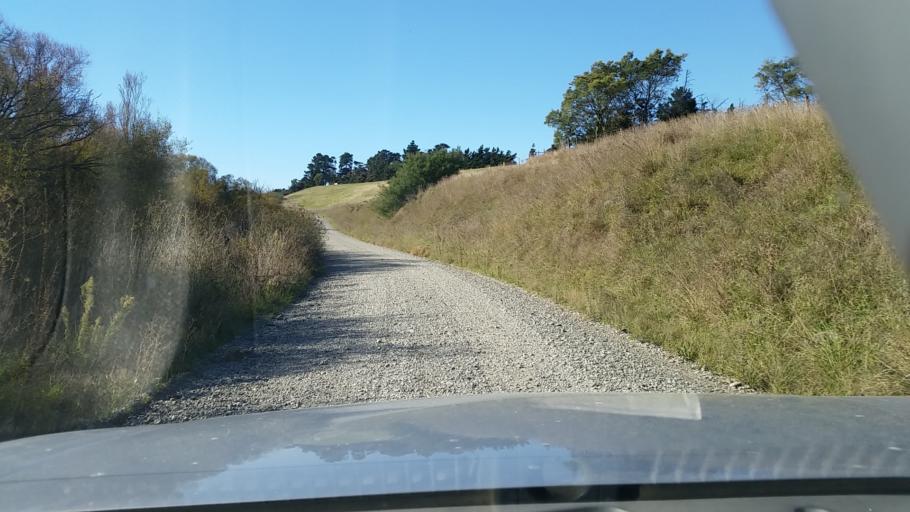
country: NZ
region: Marlborough
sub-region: Marlborough District
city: Blenheim
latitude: -41.6781
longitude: 174.1419
